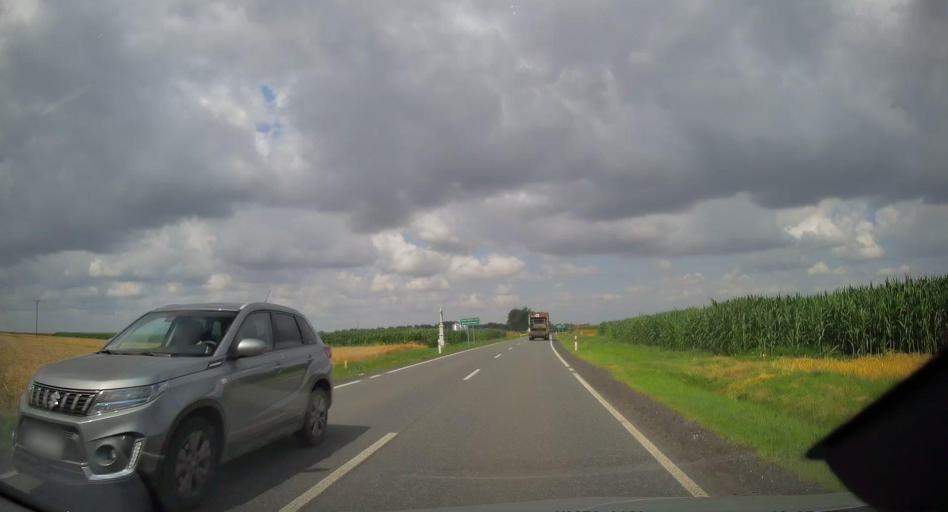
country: PL
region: Opole Voivodeship
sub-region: Powiat prudnicki
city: Glogowek
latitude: 50.3456
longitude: 17.8922
